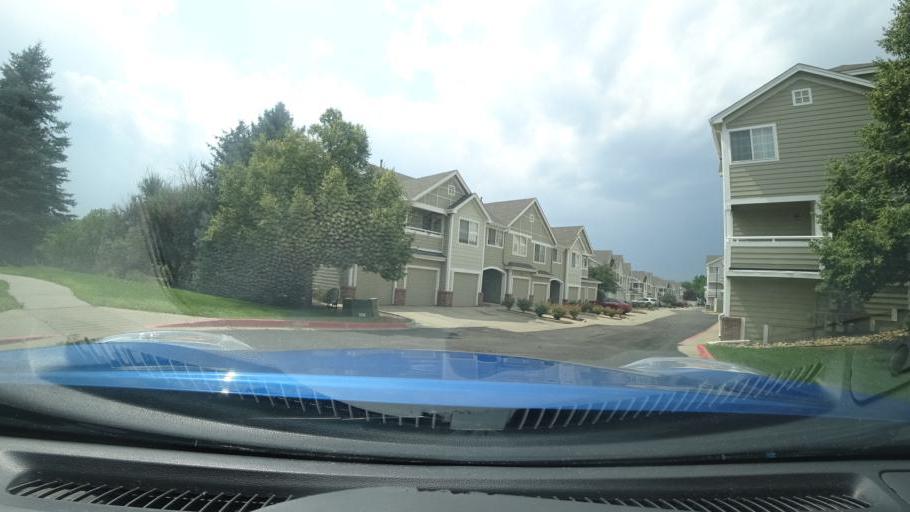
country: US
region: Colorado
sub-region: Adams County
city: Aurora
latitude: 39.6906
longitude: -104.7649
